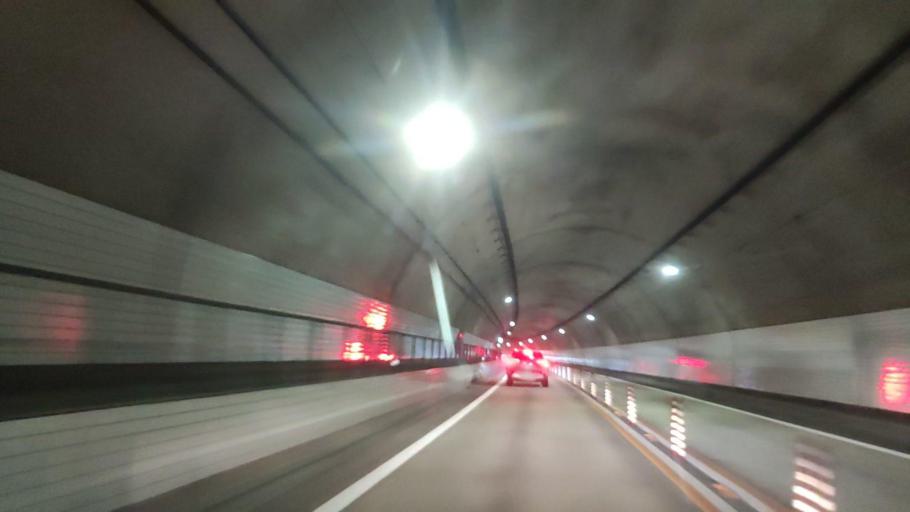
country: JP
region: Kyoto
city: Miyazu
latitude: 35.5575
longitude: 135.1251
